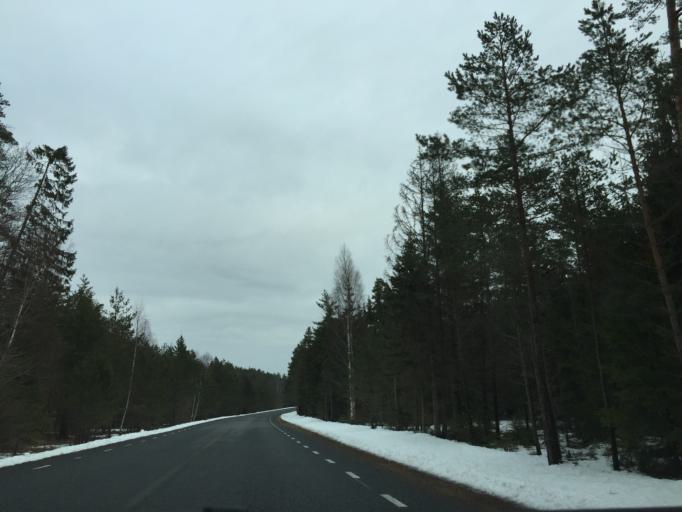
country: EE
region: Saare
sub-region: Kuressaare linn
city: Kuressaare
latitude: 58.4347
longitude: 22.2146
